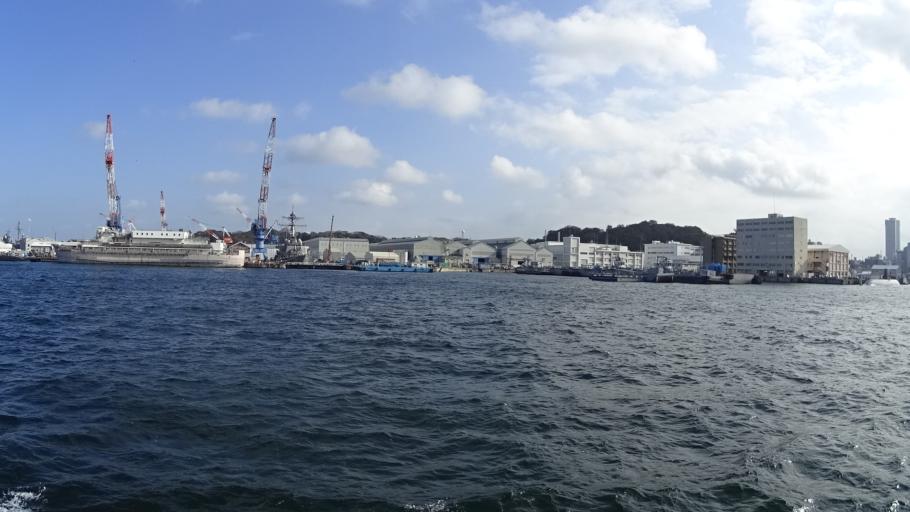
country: JP
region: Kanagawa
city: Yokosuka
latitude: 35.2872
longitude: 139.6566
